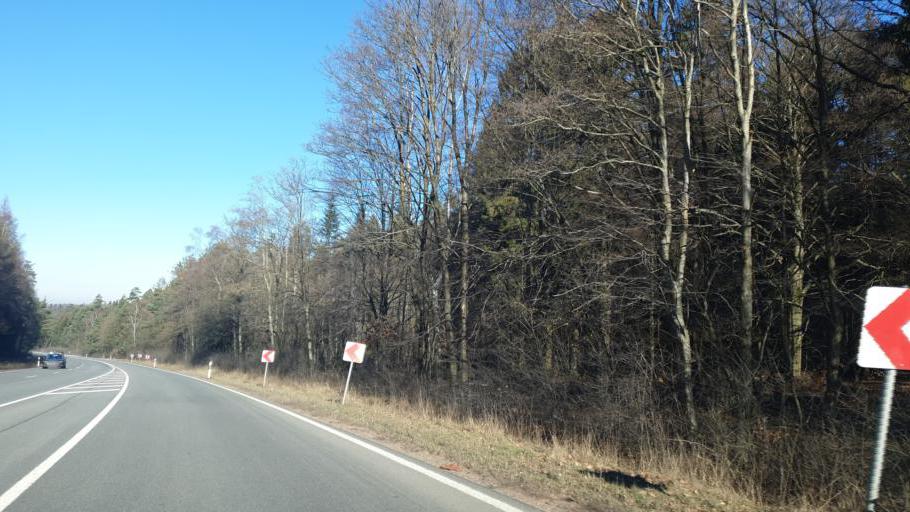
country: DE
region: Hesse
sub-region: Regierungsbezirk Darmstadt
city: Wiesbaden
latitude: 50.1391
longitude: 8.2191
